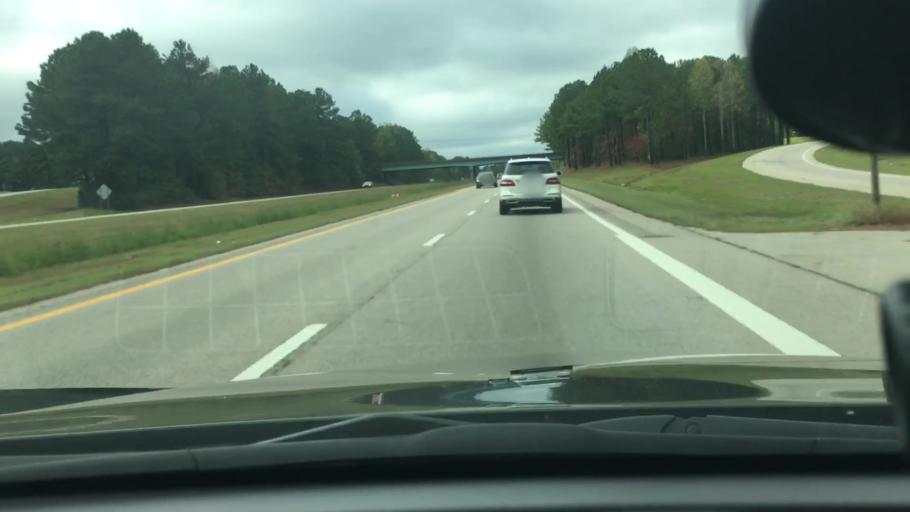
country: US
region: North Carolina
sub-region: Wake County
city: Zebulon
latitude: 35.8200
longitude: -78.2656
